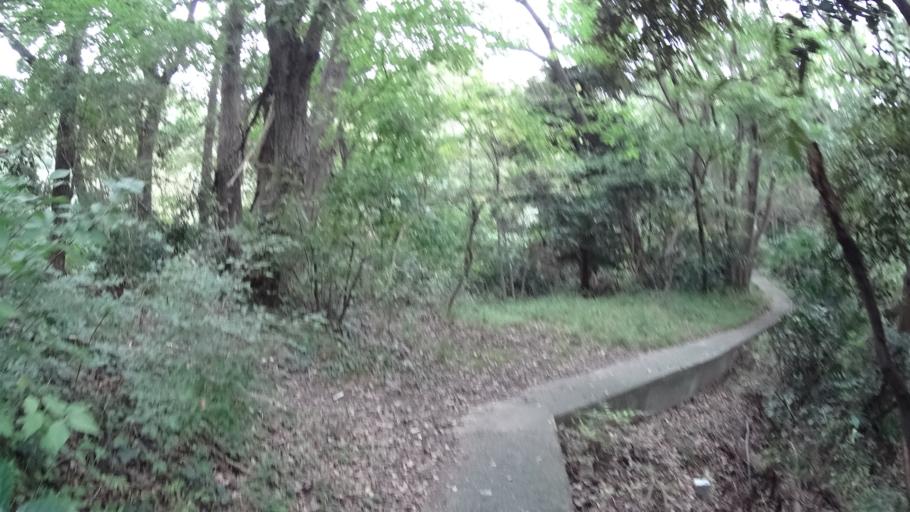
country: JP
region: Kanagawa
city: Yokosuka
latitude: 35.3062
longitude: 139.6264
